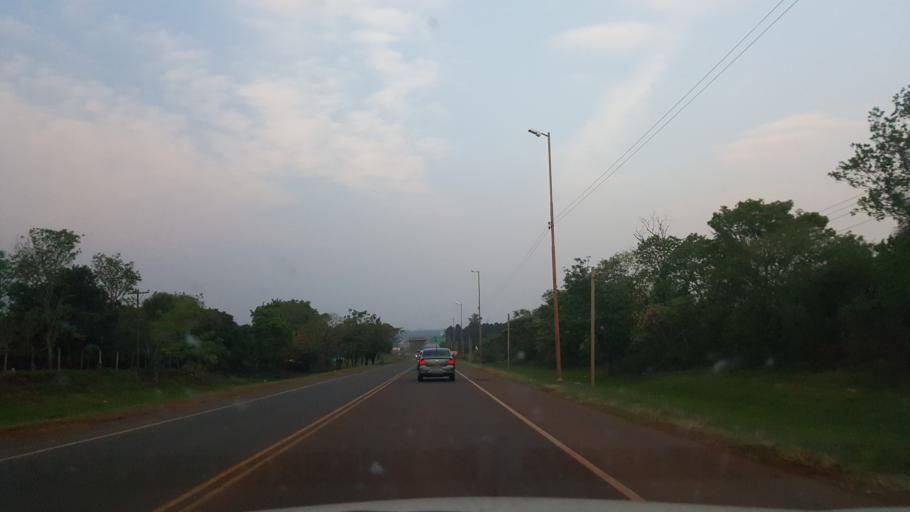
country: AR
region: Misiones
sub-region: Departamento de Capital
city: Posadas
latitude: -27.4043
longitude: -55.9700
